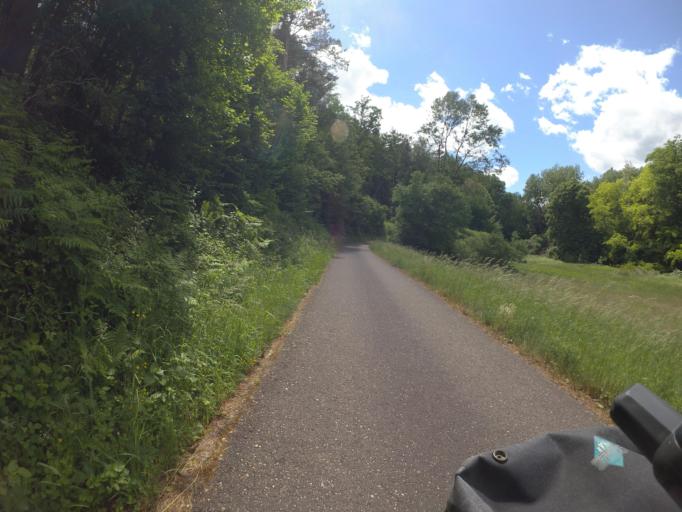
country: DE
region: Rheinland-Pfalz
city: Rumbach
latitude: 49.0843
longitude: 7.7901
